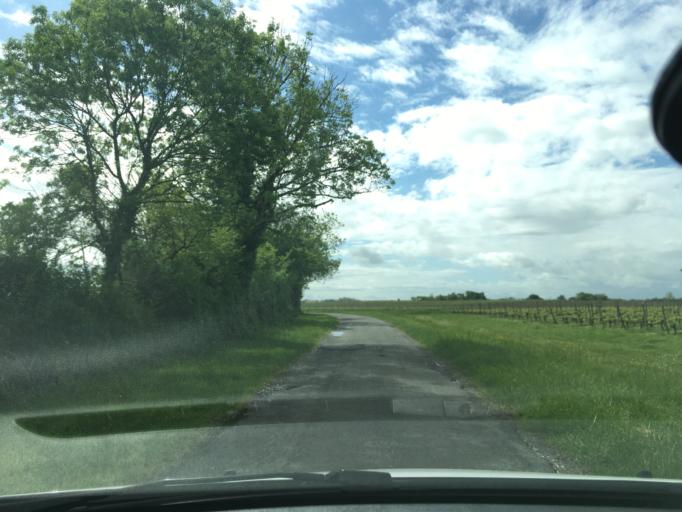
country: FR
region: Aquitaine
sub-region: Departement de la Gironde
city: Saint-Estephe
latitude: 45.3275
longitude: -0.8047
